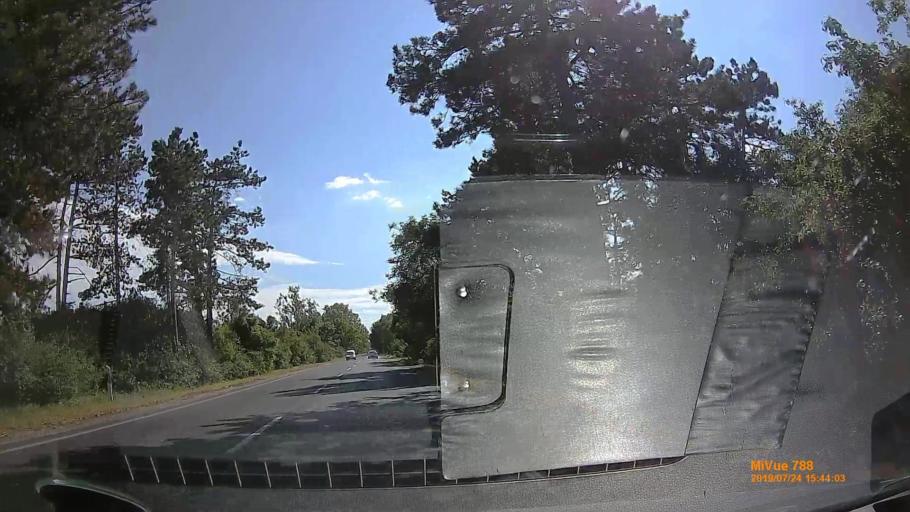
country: HU
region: Szabolcs-Szatmar-Bereg
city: Vasarosnameny
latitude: 48.1047
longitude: 22.2996
